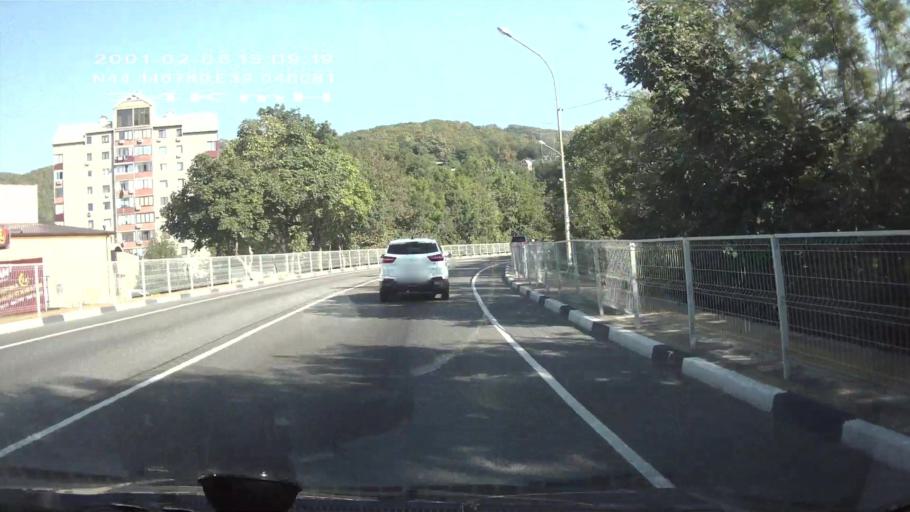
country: RU
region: Krasnodarskiy
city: Agoy
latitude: 44.1468
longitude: 39.0401
